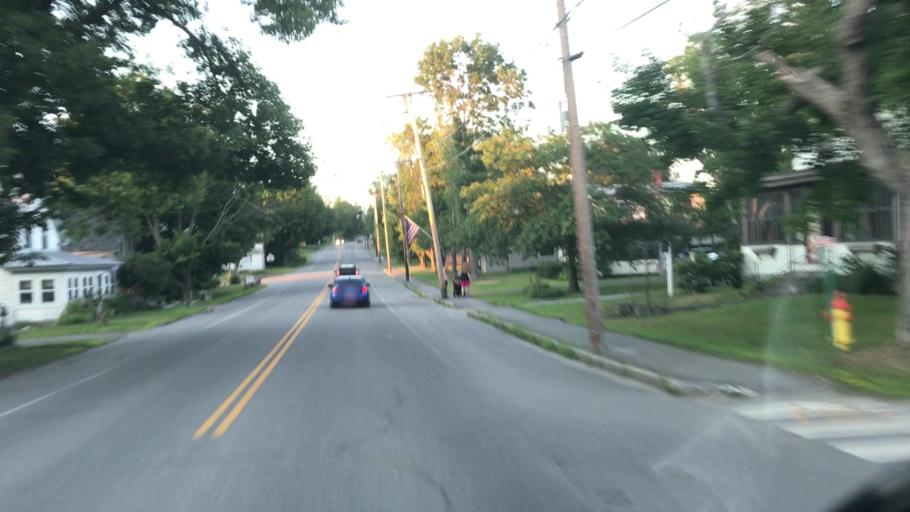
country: US
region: Maine
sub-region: Penobscot County
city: Lincoln
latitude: 45.3665
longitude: -68.5014
